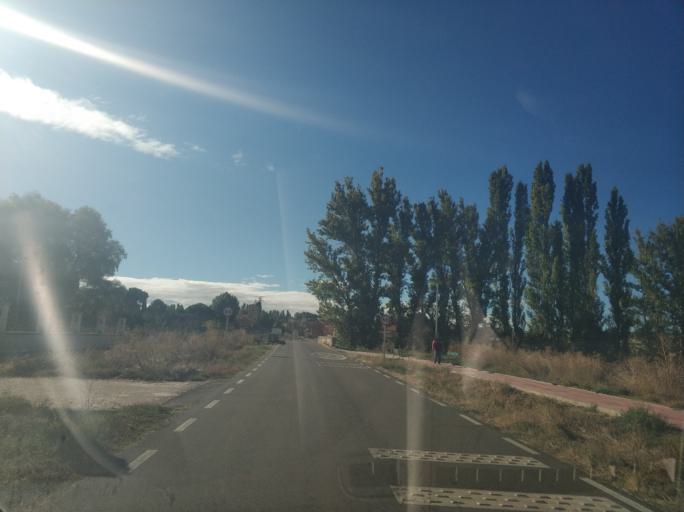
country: ES
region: Castille and Leon
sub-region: Provincia de Burgos
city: San Juan del Monte
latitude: 41.6871
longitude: -3.5219
